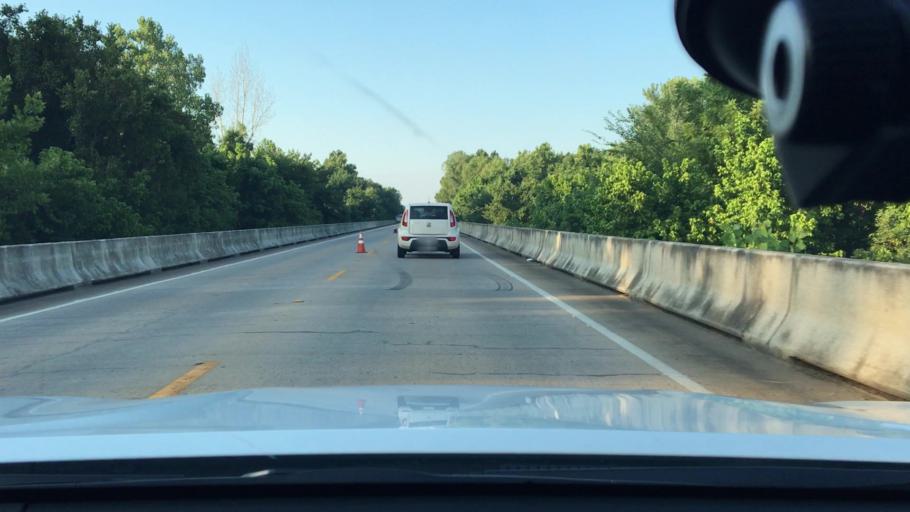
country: US
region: Arkansas
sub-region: Johnson County
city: Clarksville
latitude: 35.4042
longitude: -93.5314
